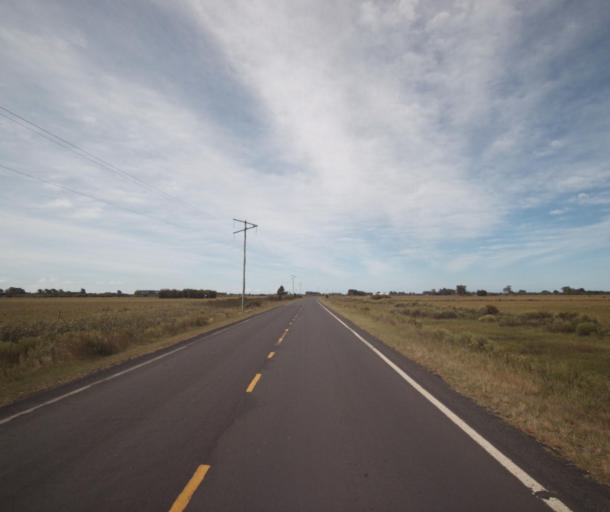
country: BR
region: Rio Grande do Sul
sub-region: Rio Grande
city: Rio Grande
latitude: -31.9299
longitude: -51.9604
